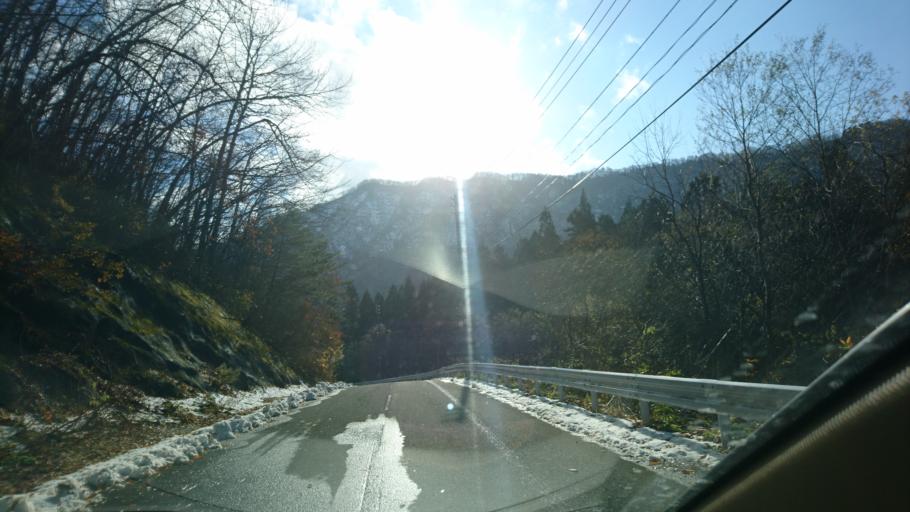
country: JP
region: Iwate
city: Kitakami
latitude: 39.2932
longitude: 140.8442
